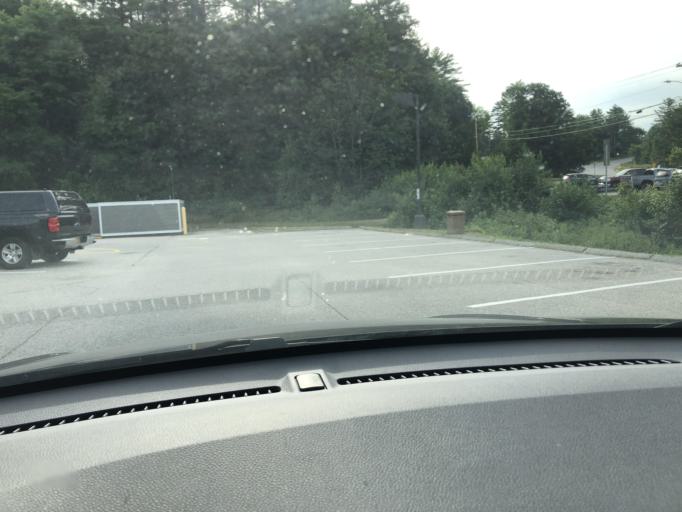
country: US
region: New Hampshire
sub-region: Merrimack County
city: Henniker
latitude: 43.2891
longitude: -71.8328
